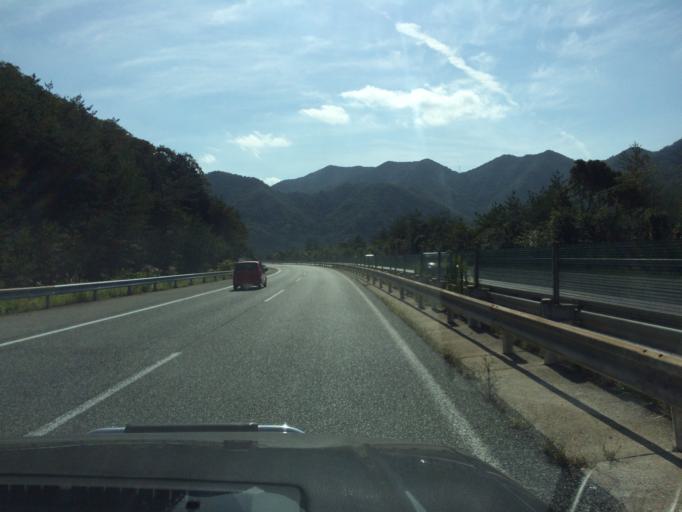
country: JP
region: Hyogo
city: Sasayama
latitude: 35.0024
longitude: 135.1574
